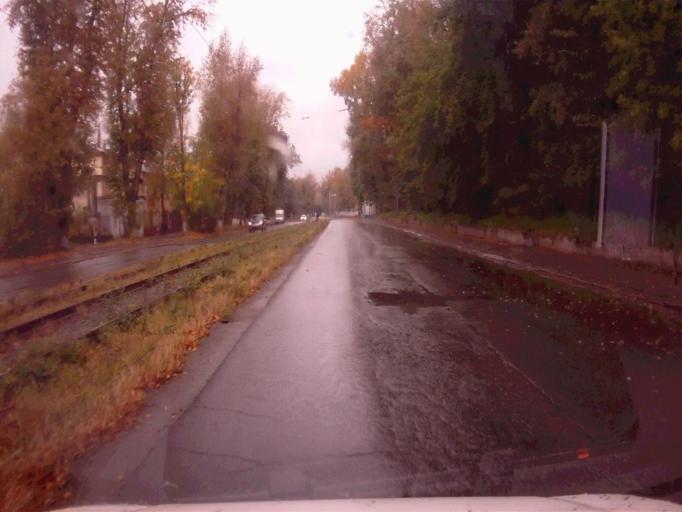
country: RU
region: Chelyabinsk
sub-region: Gorod Chelyabinsk
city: Chelyabinsk
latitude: 55.1896
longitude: 61.4128
